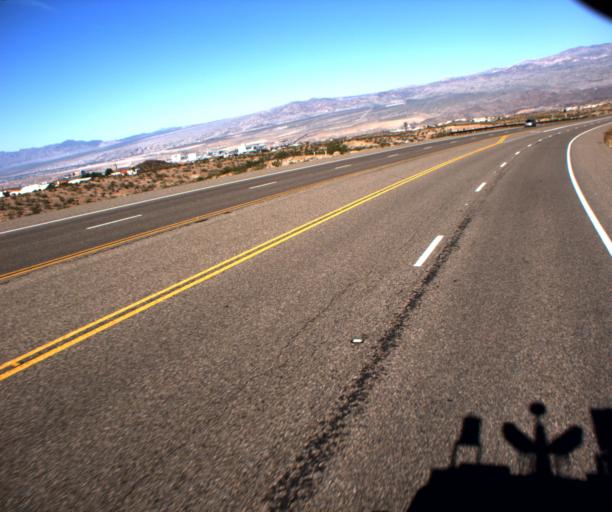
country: US
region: Nevada
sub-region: Clark County
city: Laughlin
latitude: 35.1848
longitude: -114.4975
